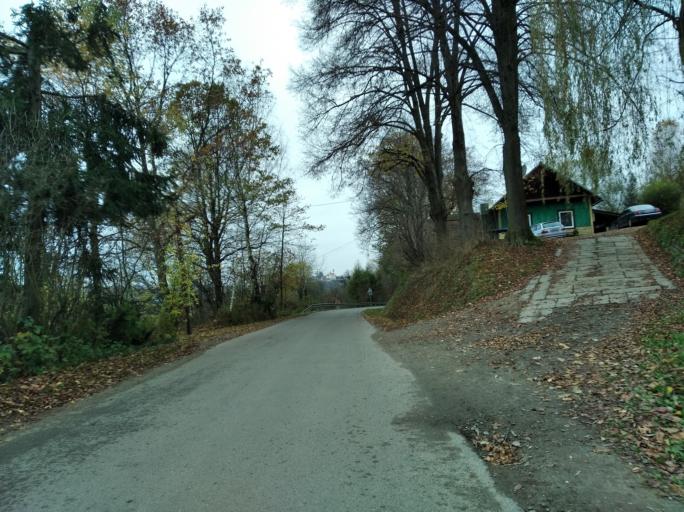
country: PL
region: Subcarpathian Voivodeship
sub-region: Powiat strzyzowski
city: Frysztak
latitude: 49.8295
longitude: 21.6338
